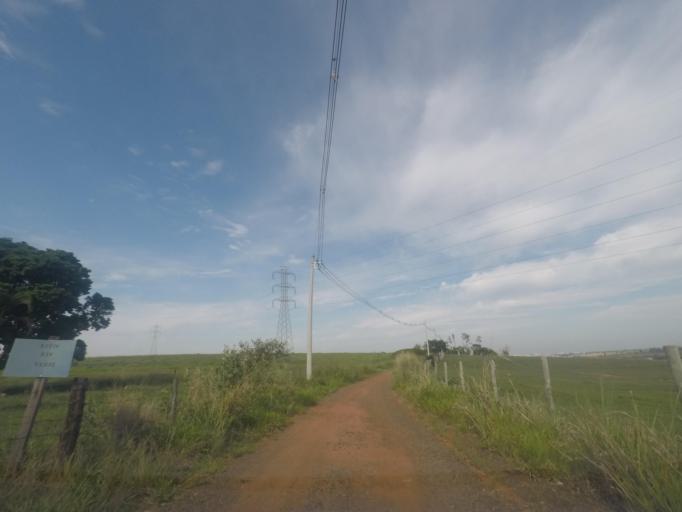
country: BR
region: Sao Paulo
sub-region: Sumare
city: Sumare
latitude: -22.7856
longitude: -47.2351
